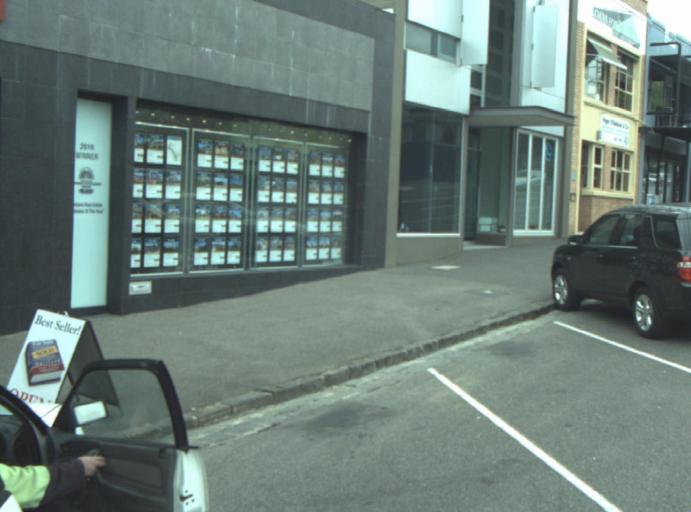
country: AU
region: Victoria
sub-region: Greater Geelong
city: Geelong
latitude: -38.1490
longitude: 144.3572
